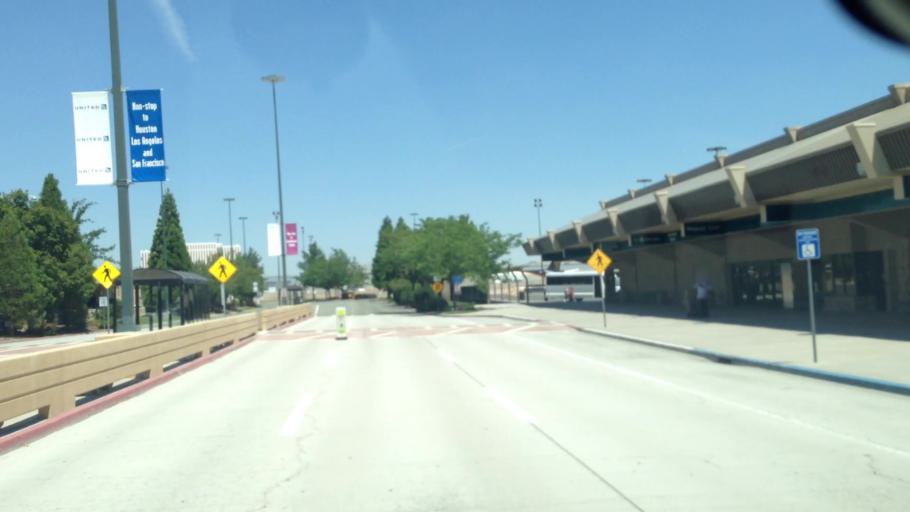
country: US
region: Nevada
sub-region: Washoe County
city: Sparks
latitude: 39.5064
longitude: -119.7758
